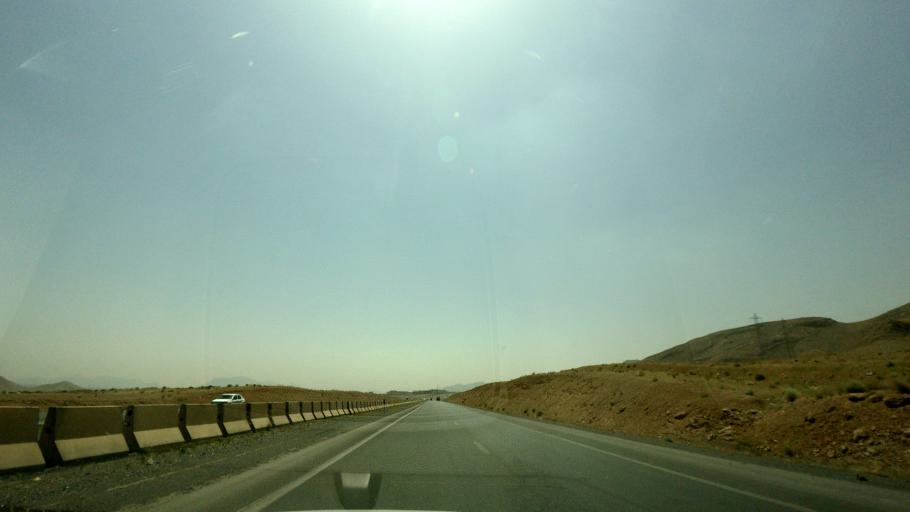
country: IR
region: Isfahan
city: Najafabad
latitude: 32.5385
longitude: 51.3200
